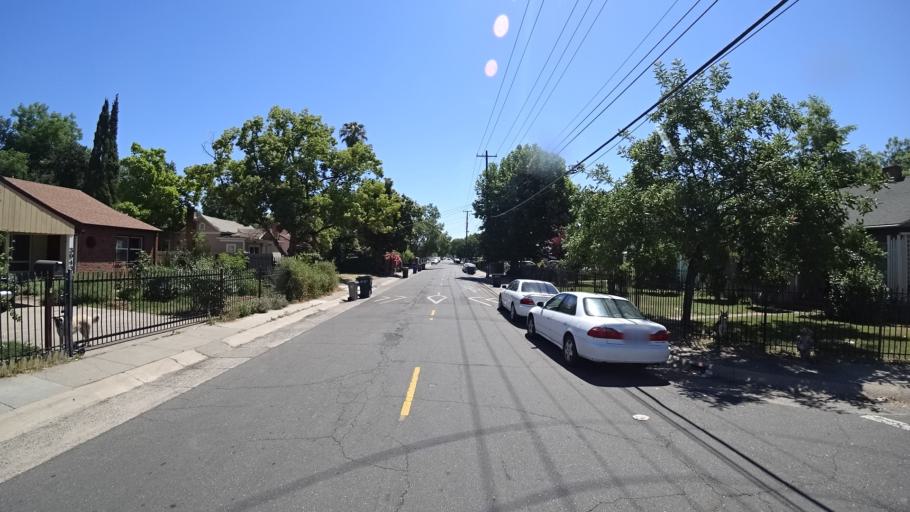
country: US
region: California
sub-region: Sacramento County
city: Parkway
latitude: 38.5412
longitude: -121.4627
